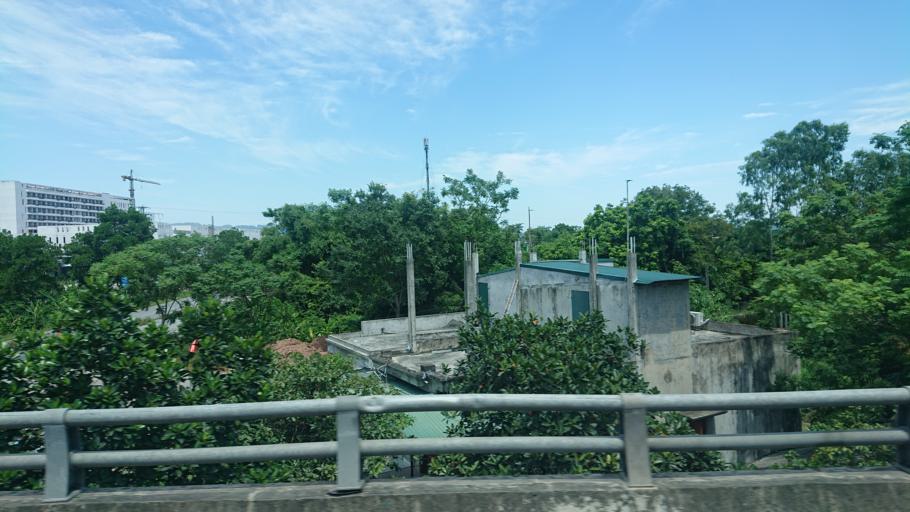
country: VN
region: Ha Nam
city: Thanh Pho Phu Ly
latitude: 20.5433
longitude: 105.9479
